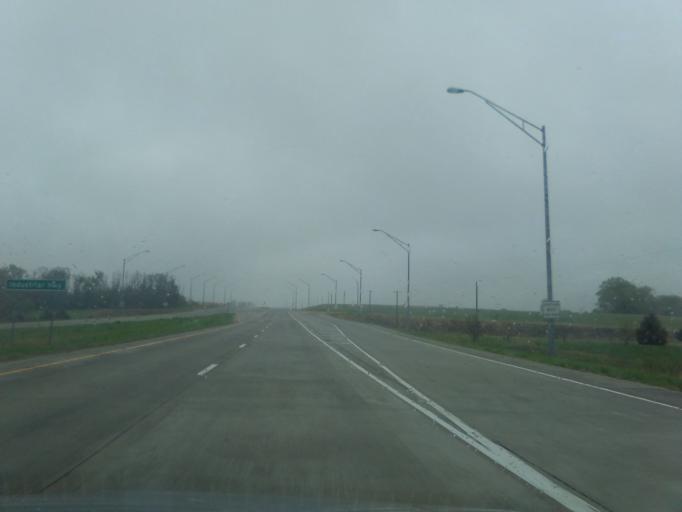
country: US
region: Nebraska
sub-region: Madison County
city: Norfolk
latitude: 42.0679
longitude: -97.3420
